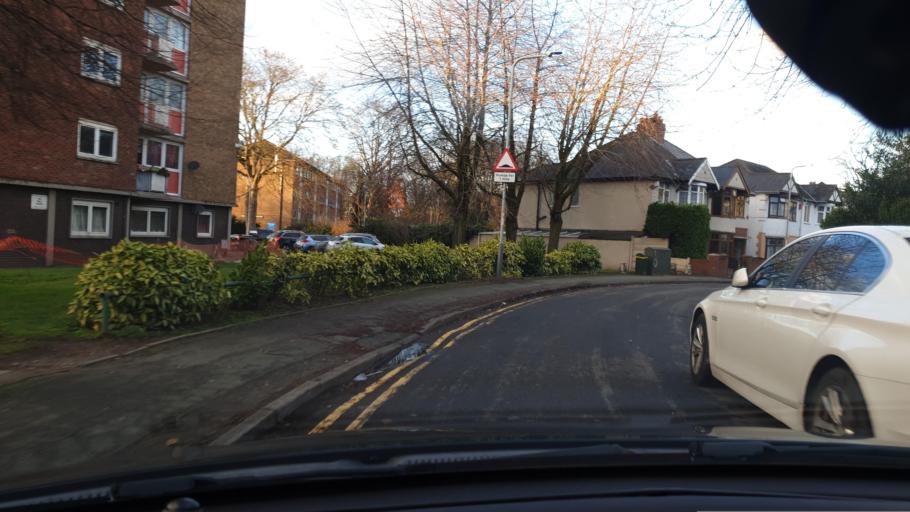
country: GB
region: England
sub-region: Wolverhampton
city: Wolverhampton
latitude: 52.5889
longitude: -2.1442
